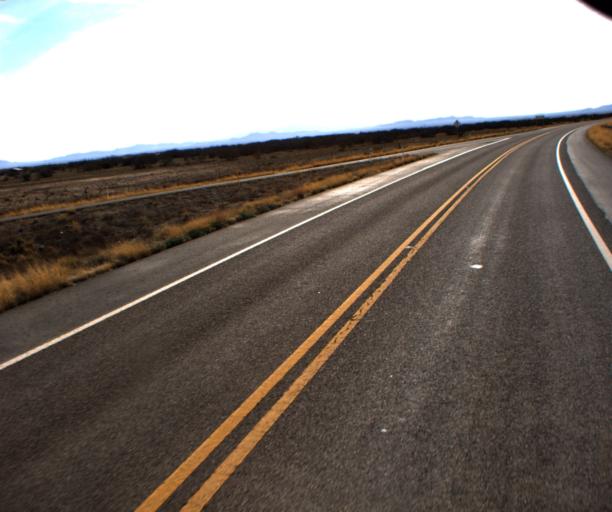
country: US
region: Arizona
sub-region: Cochise County
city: Willcox
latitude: 32.1953
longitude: -109.7568
